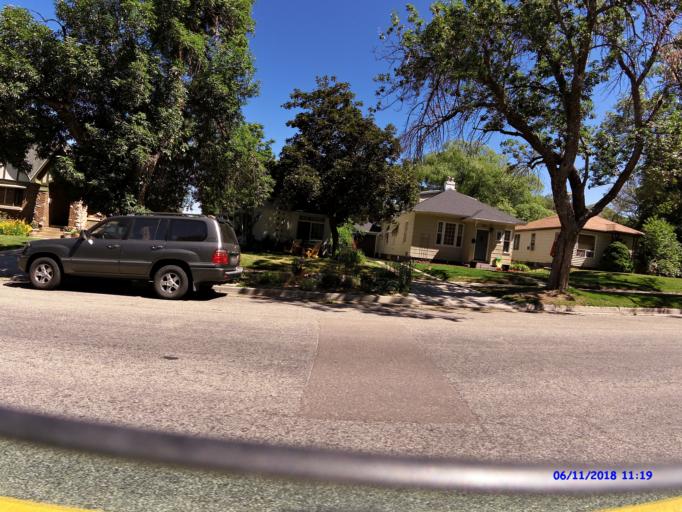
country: US
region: Utah
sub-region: Weber County
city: Ogden
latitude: 41.2224
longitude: -111.9433
